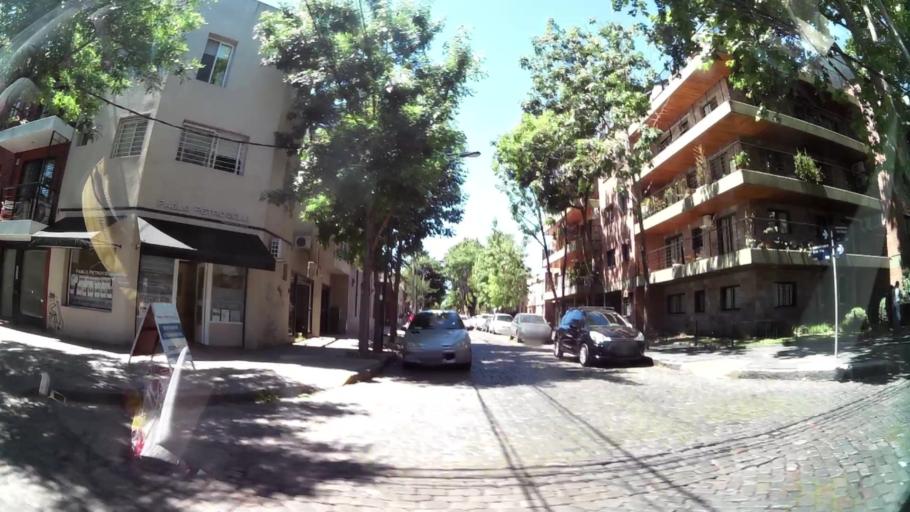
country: AR
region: Buenos Aires
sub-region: Partido de San Isidro
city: San Isidro
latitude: -34.4711
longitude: -58.5226
